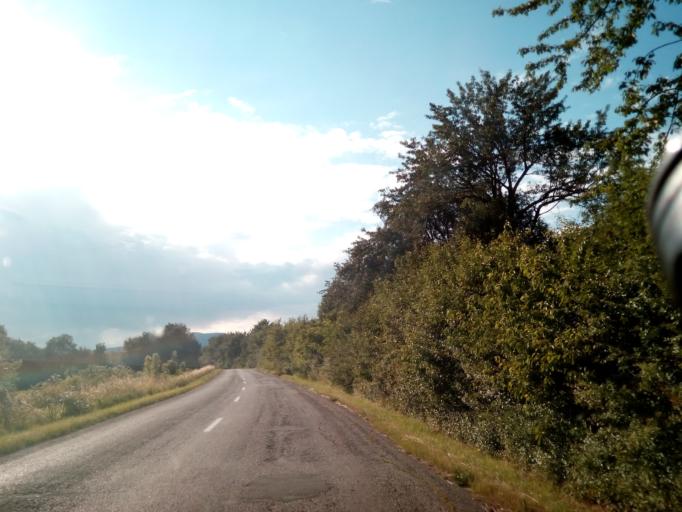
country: SK
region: Kosicky
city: Secovce
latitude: 48.6104
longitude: 21.5496
